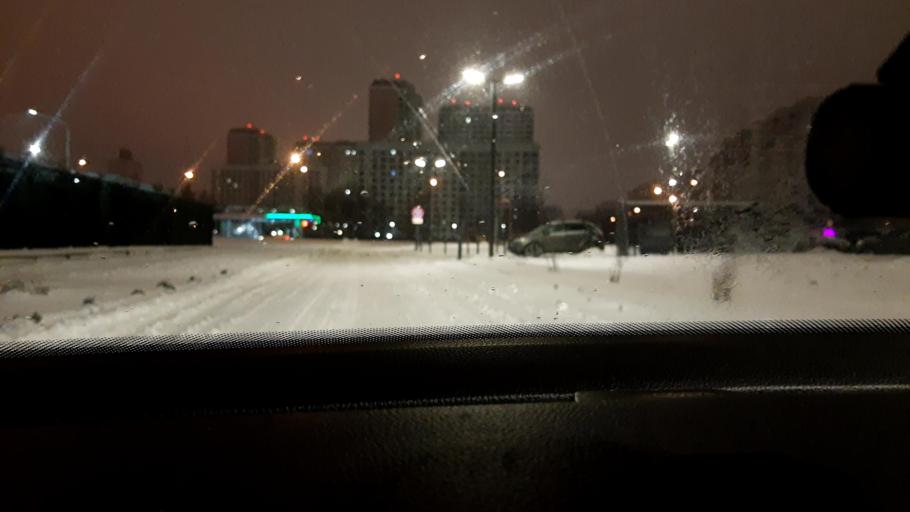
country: RU
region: Moscow
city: Orekhovo-Borisovo
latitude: 55.6011
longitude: 37.7267
